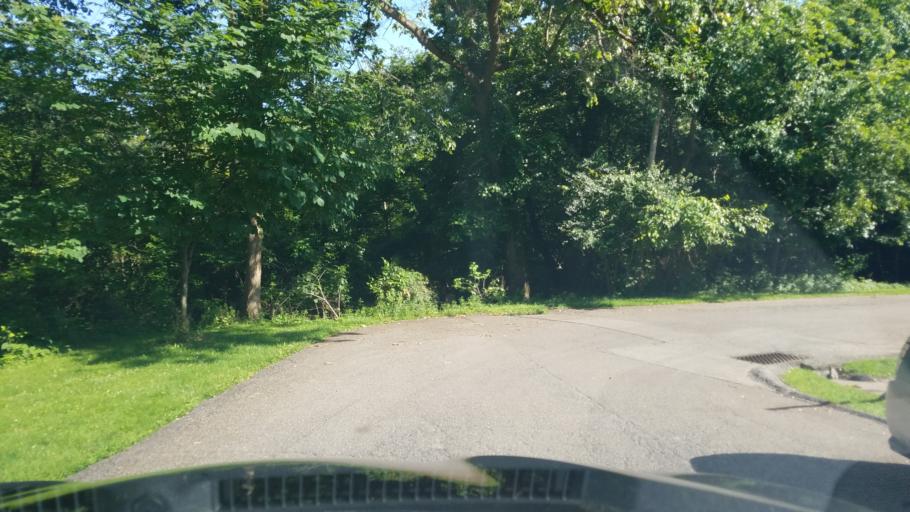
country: US
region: Pennsylvania
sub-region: Allegheny County
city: Swissvale
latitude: 40.4306
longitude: -79.8989
